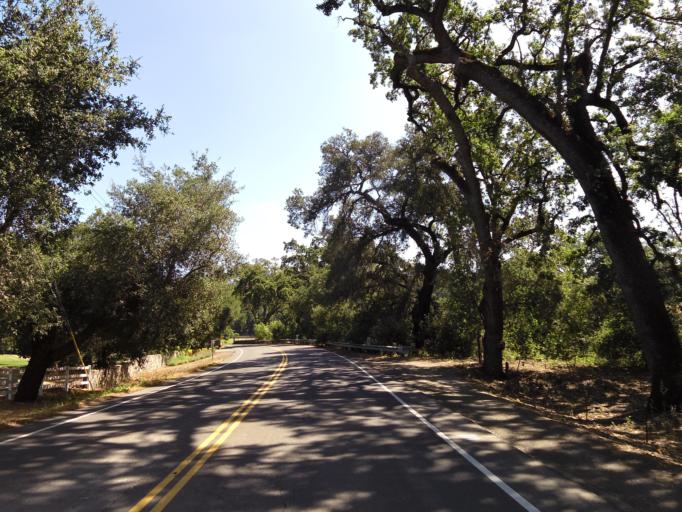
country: US
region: California
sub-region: Napa County
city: Saint Helena
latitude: 38.4945
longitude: -122.4265
